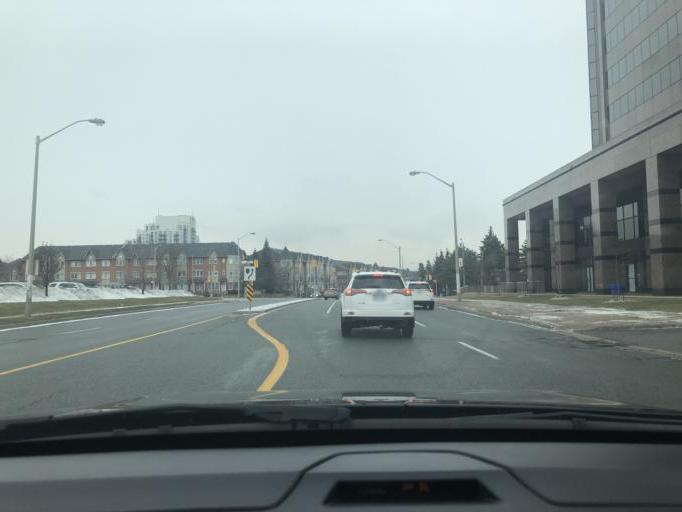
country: CA
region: Ontario
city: Scarborough
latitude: 43.7893
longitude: -79.2337
